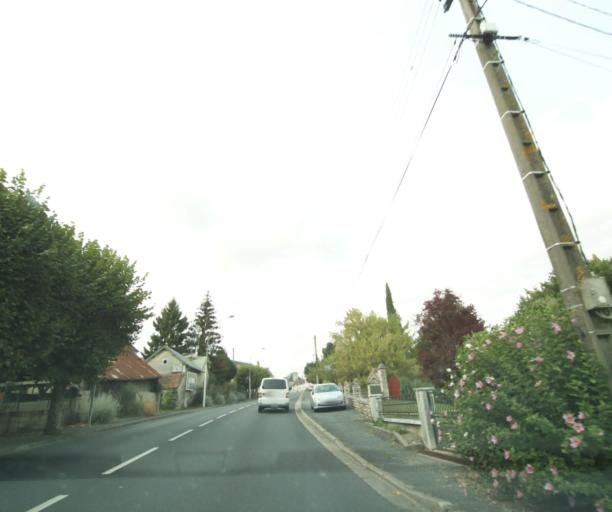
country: FR
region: Centre
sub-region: Departement de l'Indre
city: Chatillon-sur-Indre
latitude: 46.9812
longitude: 1.1766
